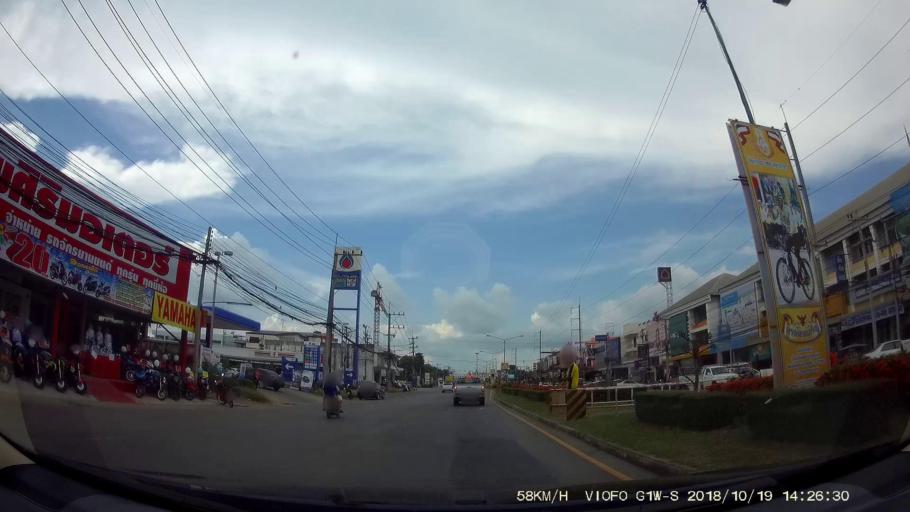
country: TH
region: Chaiyaphum
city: Kaeng Khro
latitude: 16.1068
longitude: 102.2596
